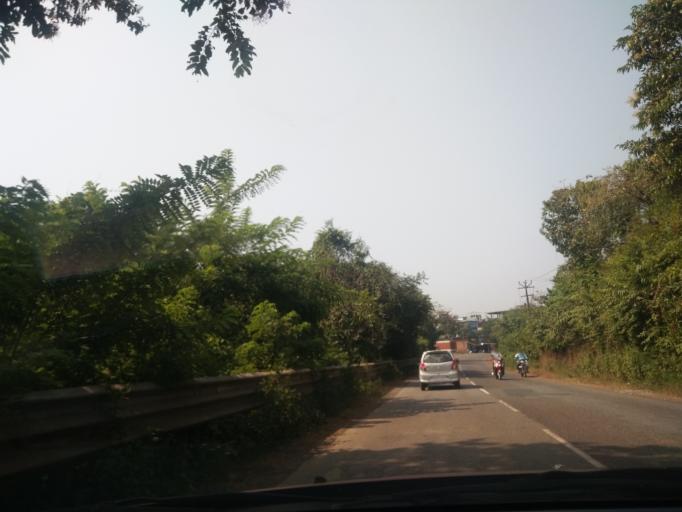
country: IN
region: Goa
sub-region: North Goa
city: Sanquelim
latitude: 15.5553
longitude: 74.0279
